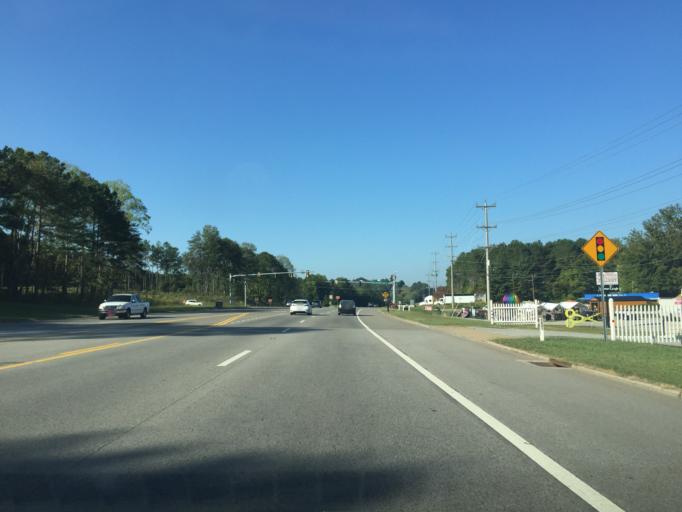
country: US
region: Tennessee
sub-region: Hamilton County
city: Harrison
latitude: 35.1089
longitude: -85.1438
